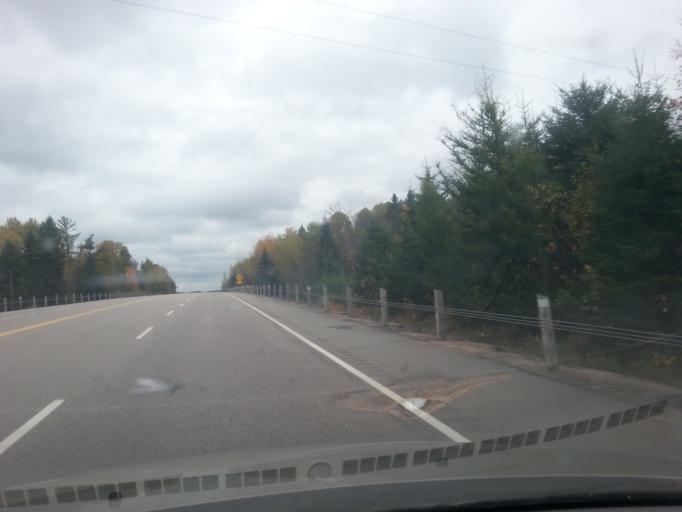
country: CA
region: Ontario
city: Mattawa
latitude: 46.2468
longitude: -78.3038
